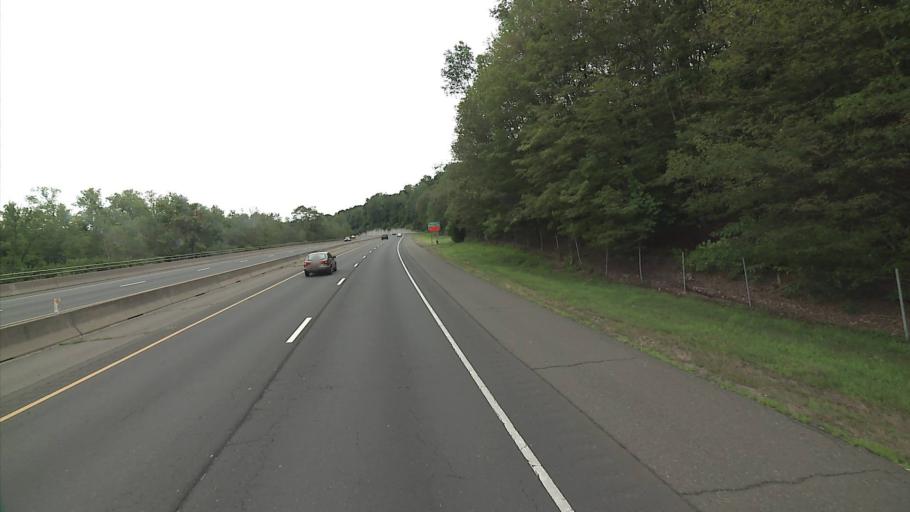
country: US
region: Connecticut
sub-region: New Haven County
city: Naugatuck
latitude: 41.4770
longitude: -73.0494
